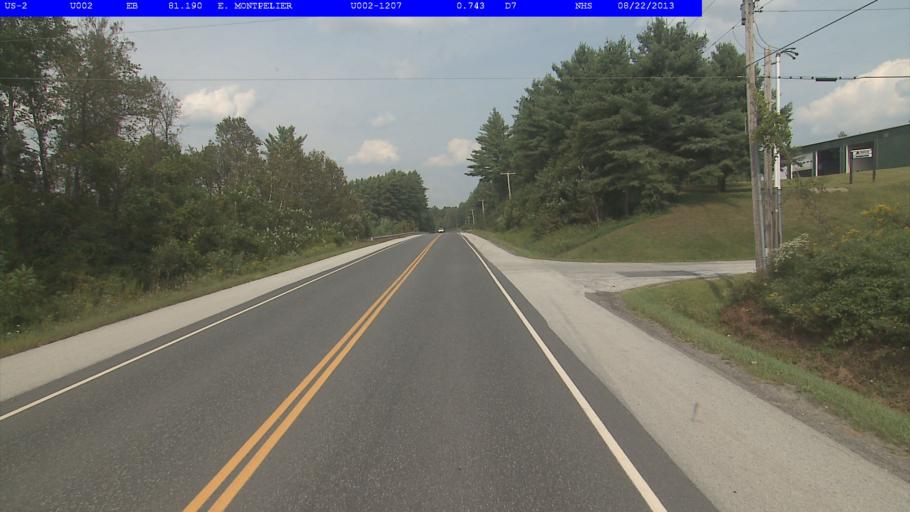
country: US
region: Vermont
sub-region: Washington County
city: Barre
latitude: 44.2445
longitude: -72.5042
